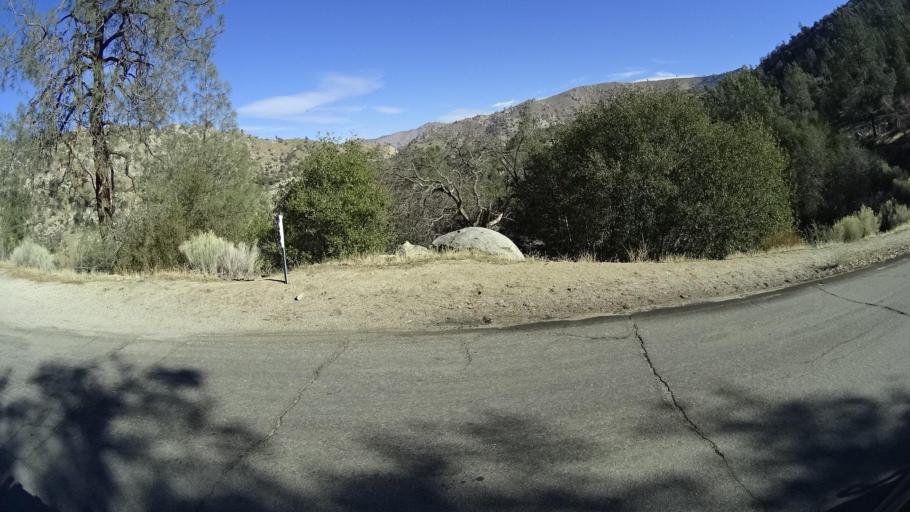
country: US
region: California
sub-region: Kern County
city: Bodfish
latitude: 35.5751
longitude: -118.5492
